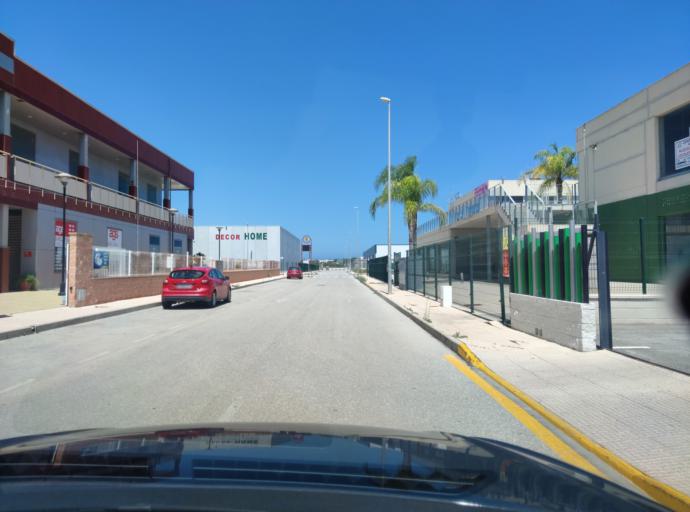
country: ES
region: Valencia
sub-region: Provincia de Alicante
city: Guardamar del Segura
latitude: 38.1173
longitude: -0.6579
